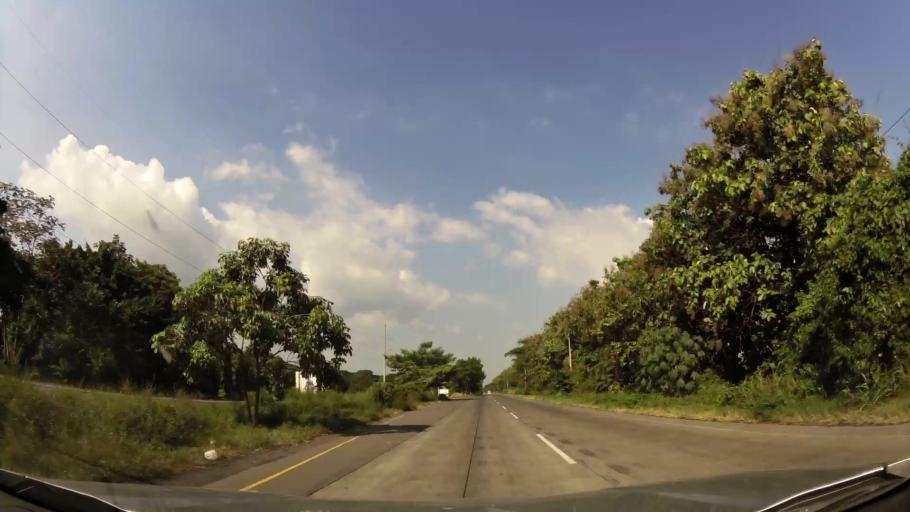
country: GT
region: Escuintla
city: Puerto San Jose
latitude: 14.0095
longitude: -90.7853
